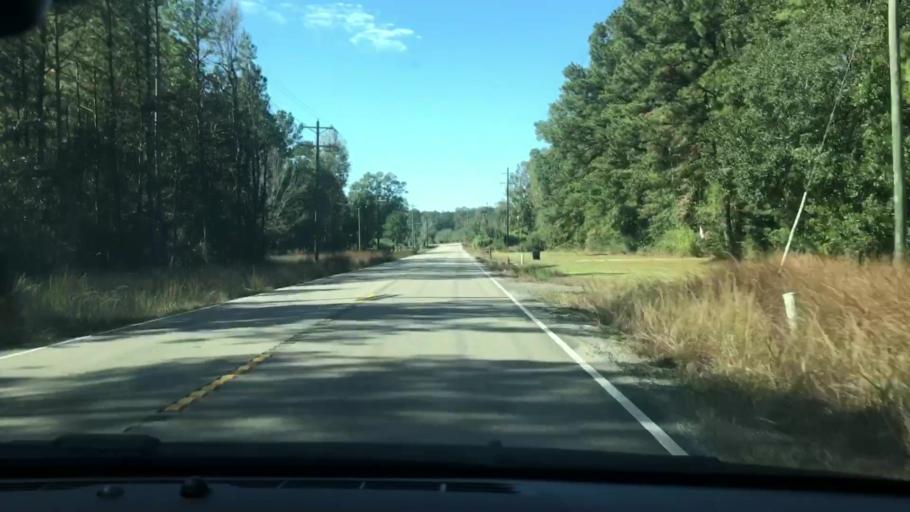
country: US
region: Louisiana
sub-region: Saint Tammany Parish
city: Abita Springs
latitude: 30.5347
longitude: -89.8951
